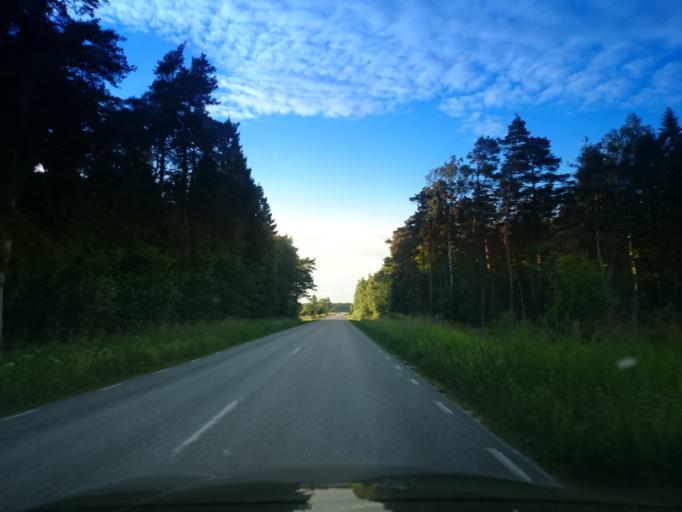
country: SE
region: Gotland
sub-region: Gotland
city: Hemse
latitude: 57.3003
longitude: 18.3832
